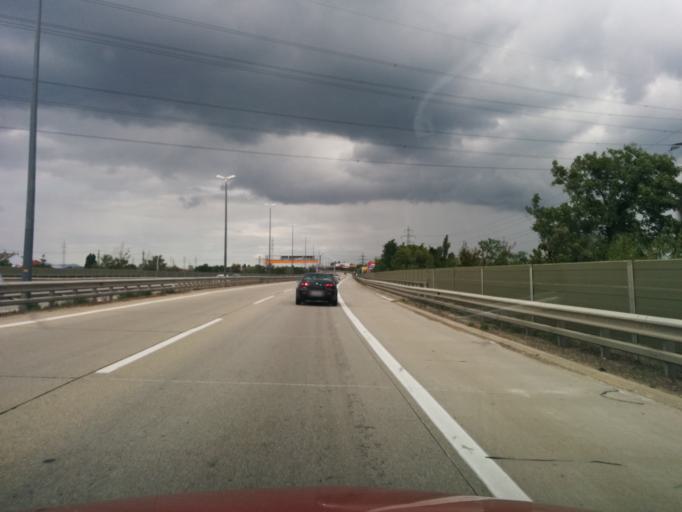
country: AT
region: Lower Austria
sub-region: Politischer Bezirk Wien-Umgebung
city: Schwechat
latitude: 48.1559
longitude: 16.4787
